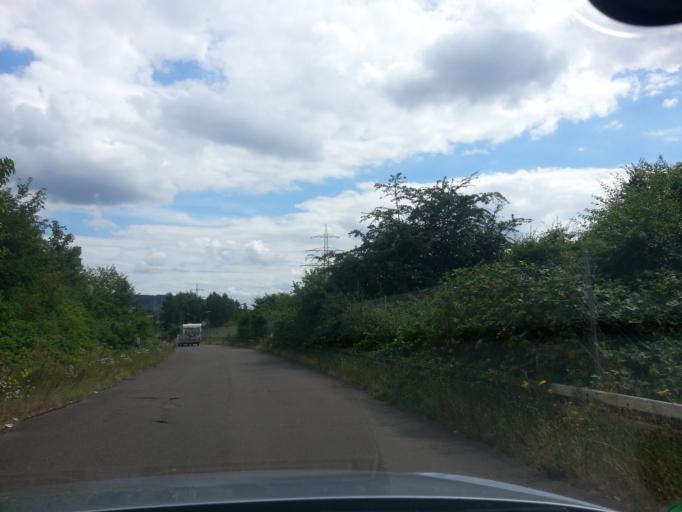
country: DE
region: Saarland
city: Merzig
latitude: 49.4595
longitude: 6.6260
